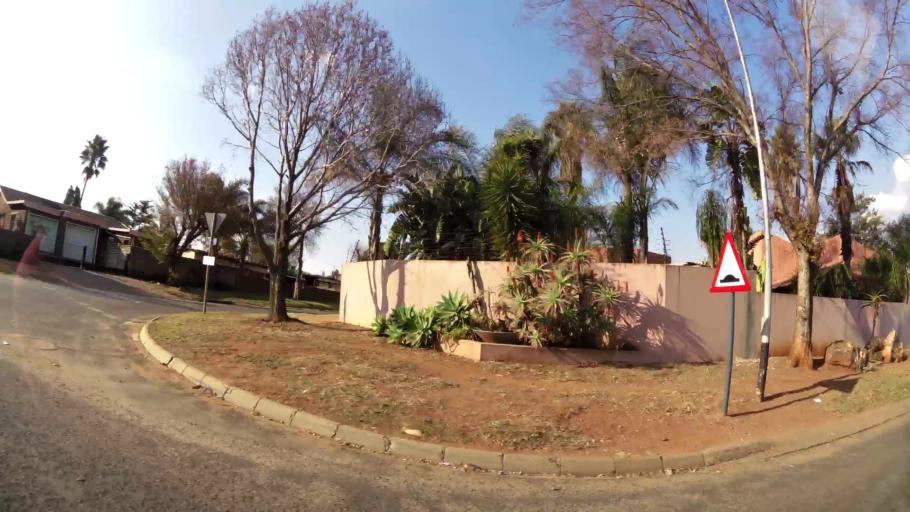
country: ZA
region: Gauteng
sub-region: Ekurhuleni Metropolitan Municipality
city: Tembisa
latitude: -25.9554
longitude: 28.2170
